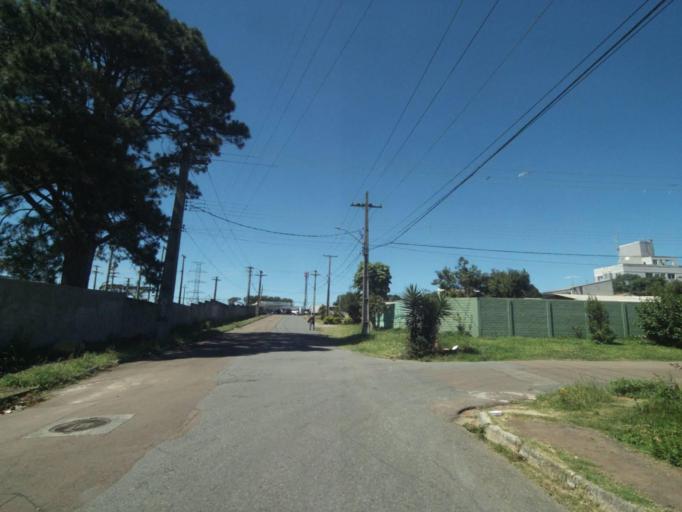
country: BR
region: Parana
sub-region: Curitiba
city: Curitiba
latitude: -25.4789
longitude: -49.3431
